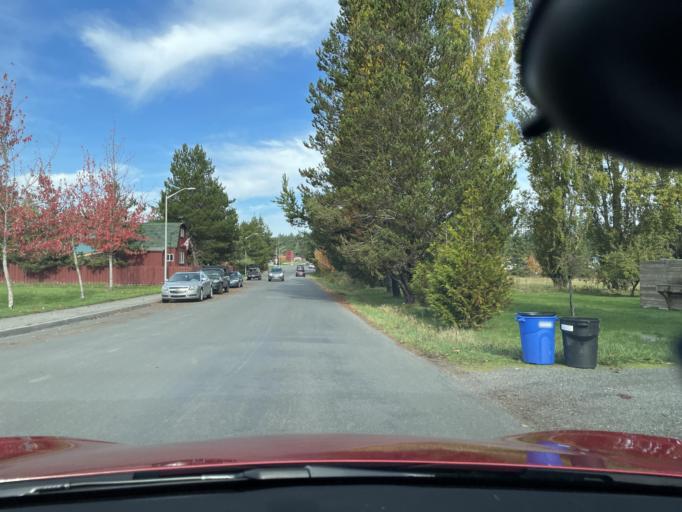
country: US
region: Washington
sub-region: San Juan County
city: Friday Harbor
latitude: 48.5386
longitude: -123.0286
